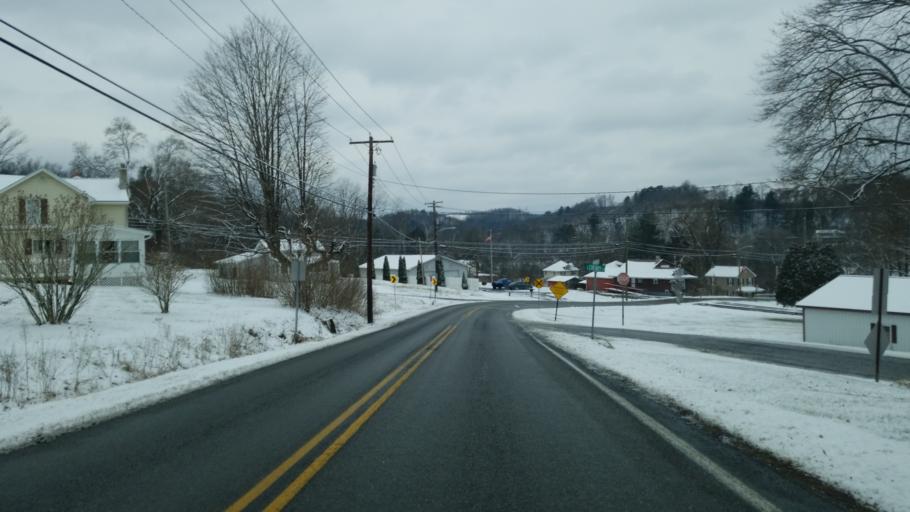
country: US
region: Pennsylvania
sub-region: Centre County
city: Stormstown
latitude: 40.7974
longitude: -78.0500
